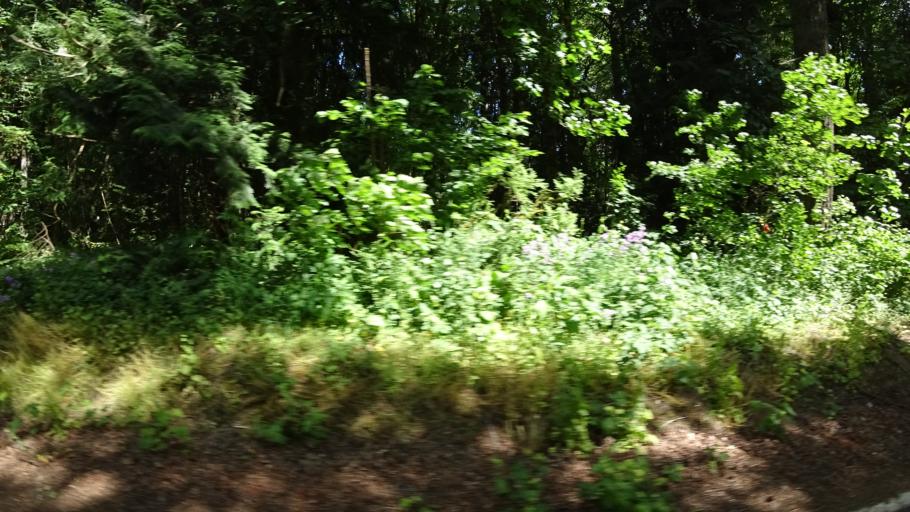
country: US
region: Oregon
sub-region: Washington County
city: Bethany
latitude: 45.6082
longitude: -122.8215
